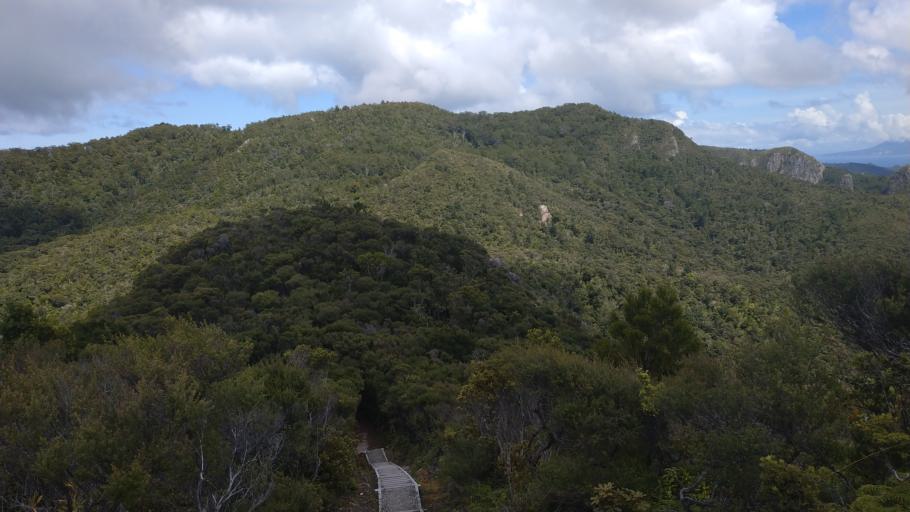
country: NZ
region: Waikato
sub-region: Thames-Coromandel District
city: Coromandel
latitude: -36.1981
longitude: 175.4087
